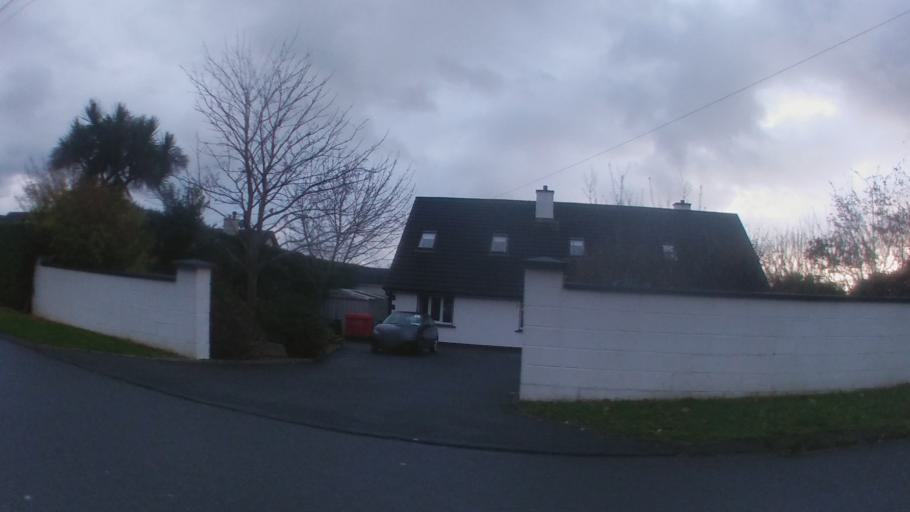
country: IE
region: Leinster
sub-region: Wicklow
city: Kilcoole
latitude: 53.1078
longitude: -6.0629
